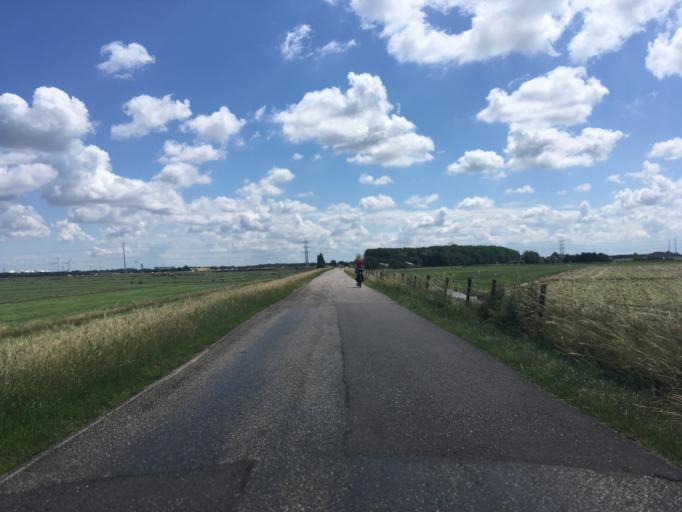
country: NL
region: North Holland
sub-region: Gemeente Haarlem
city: Haarlem
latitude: 52.4098
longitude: 4.6918
